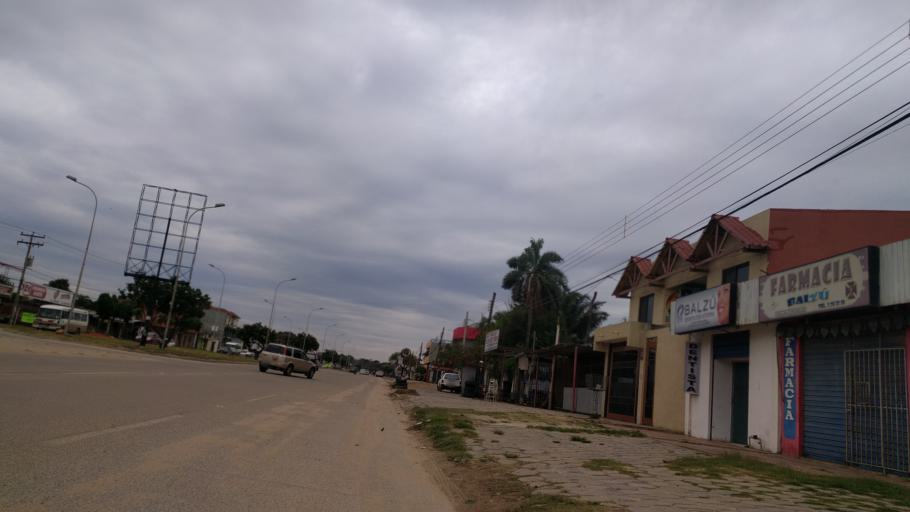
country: BO
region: Santa Cruz
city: Santa Cruz de la Sierra
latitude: -17.8384
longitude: -63.1816
